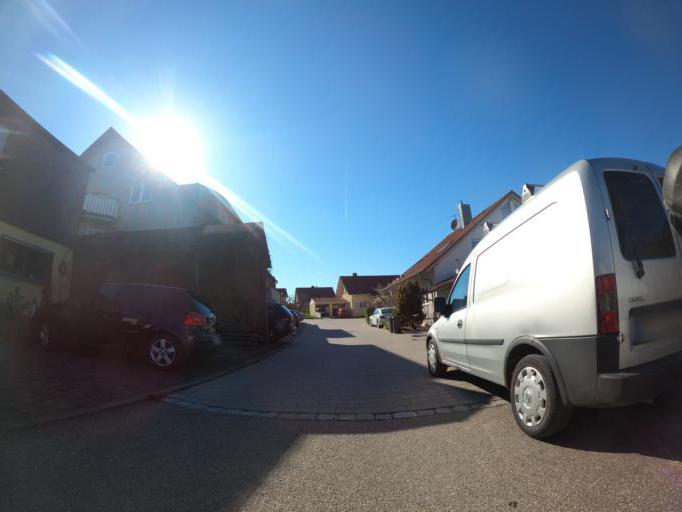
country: DE
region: Baden-Wuerttemberg
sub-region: Karlsruhe Region
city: Wimsheim
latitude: 48.8521
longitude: 8.8221
